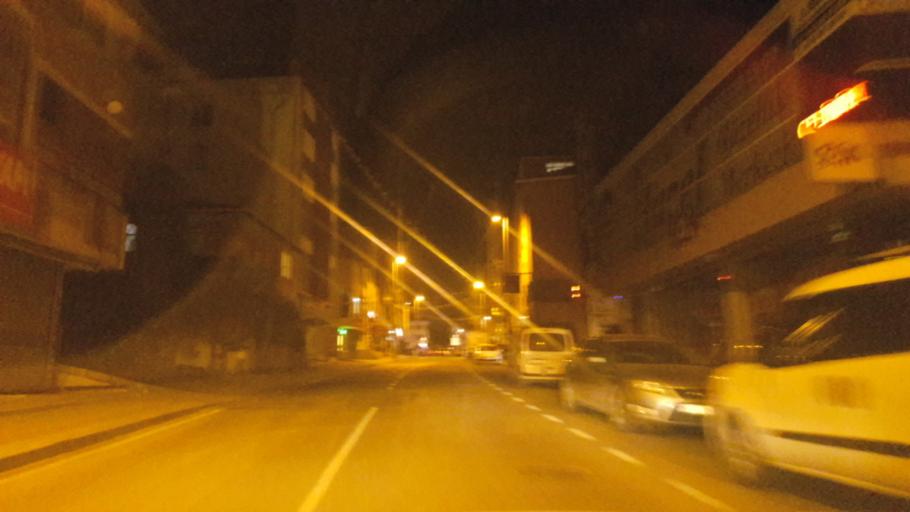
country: TR
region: Kocaeli
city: Tavsancil
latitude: 40.7859
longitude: 29.5391
